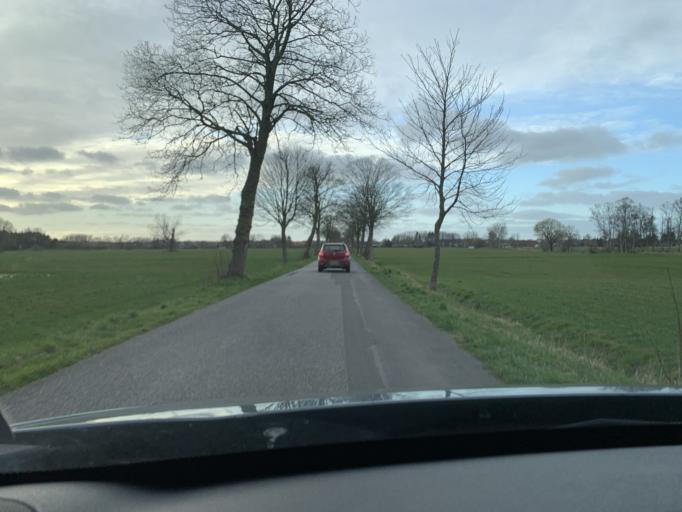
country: DE
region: Lower Saxony
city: Schwerinsdorf
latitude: 53.2681
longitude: 7.7038
